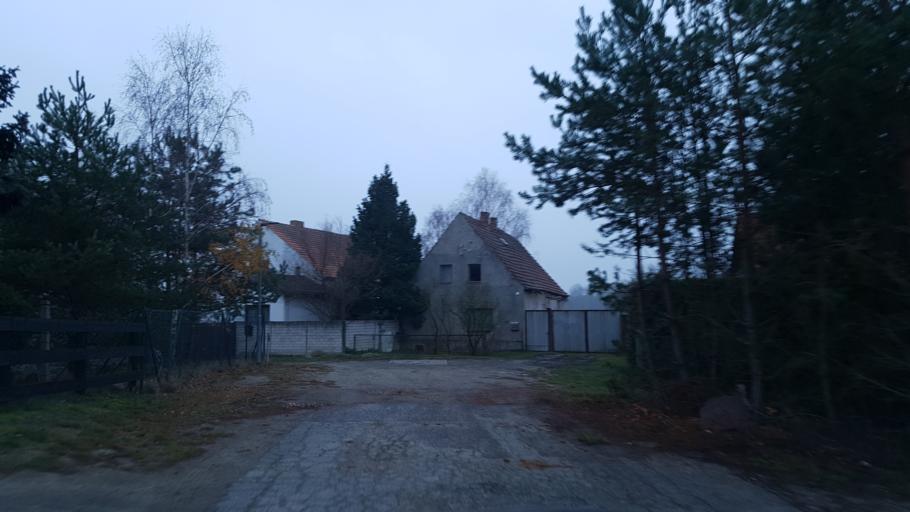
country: DE
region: Brandenburg
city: Ruckersdorf
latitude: 51.5508
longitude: 13.6022
